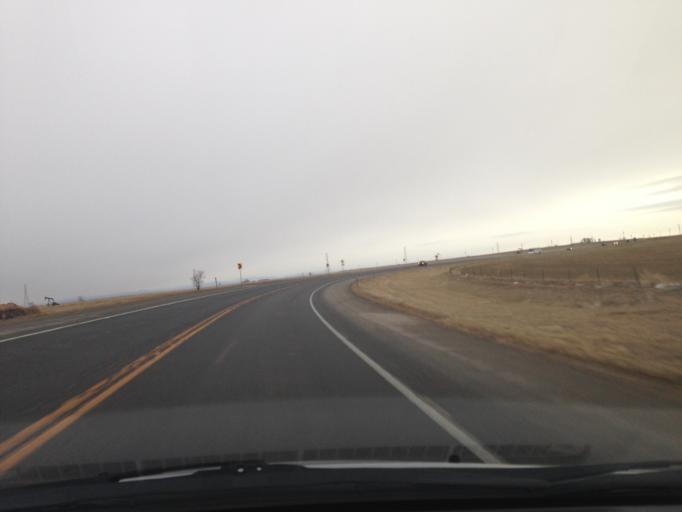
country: US
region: Colorado
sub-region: Weld County
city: Dacono
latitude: 40.0804
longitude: -104.9021
